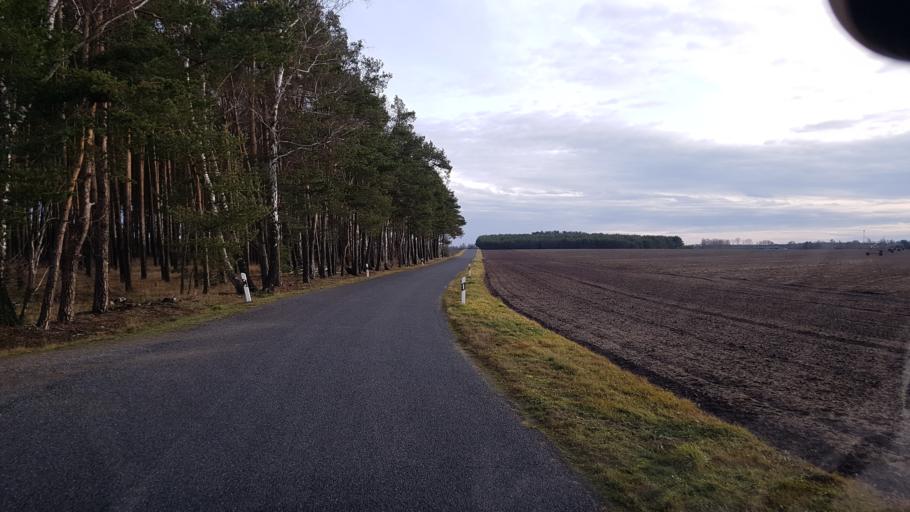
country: DE
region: Brandenburg
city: Bronkow
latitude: 51.6613
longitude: 13.8803
